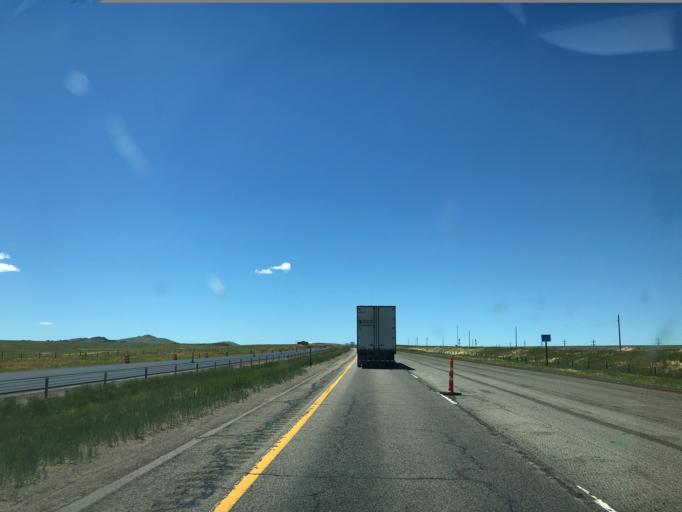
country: US
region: Wyoming
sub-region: Laramie County
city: Cheyenne
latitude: 41.0989
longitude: -105.1228
